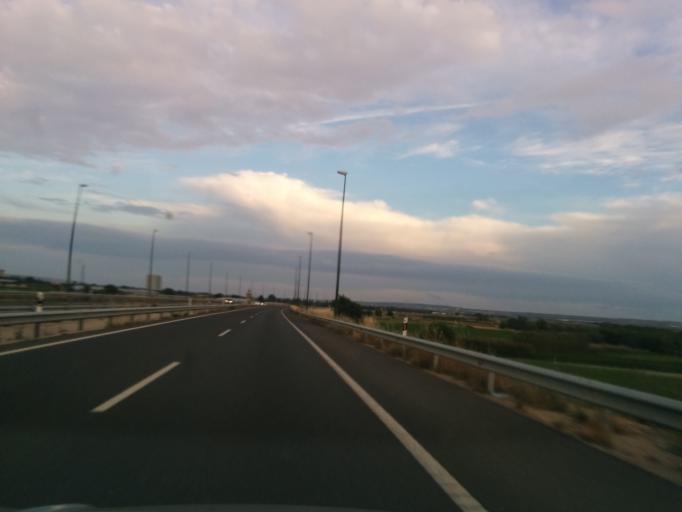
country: ES
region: Aragon
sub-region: Provincia de Zaragoza
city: Zaragoza
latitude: 41.6500
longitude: -0.8373
